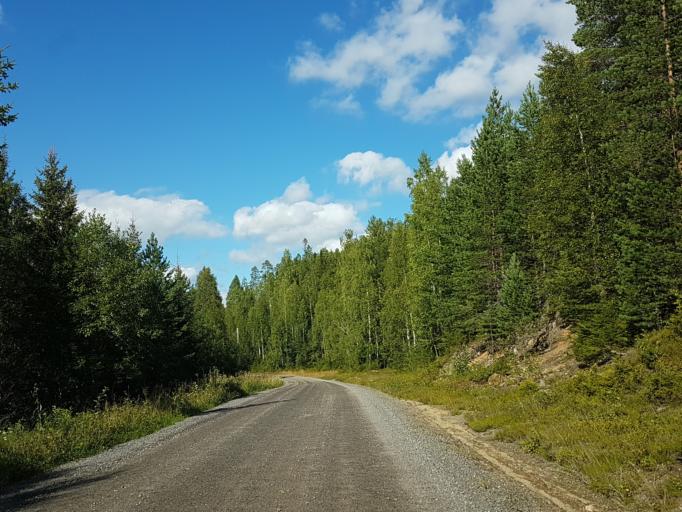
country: SE
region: Vaesterbotten
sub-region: Skelleftea Kommun
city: Burtraesk
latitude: 64.2766
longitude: 20.4795
